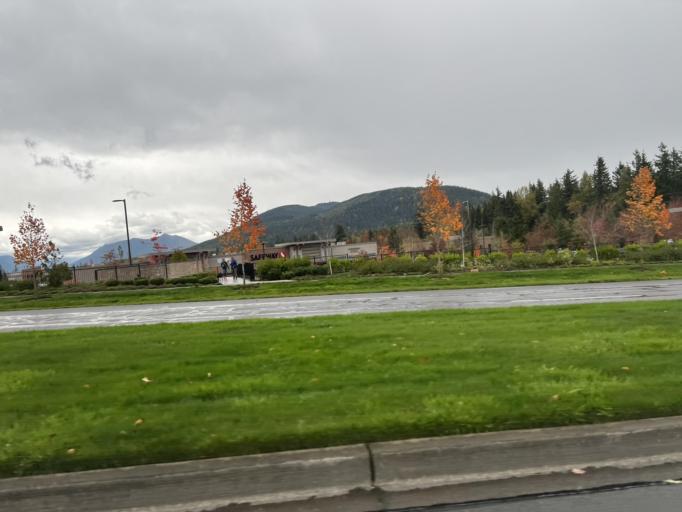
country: US
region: Washington
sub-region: King County
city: Fall City
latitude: 47.5285
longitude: -121.8750
